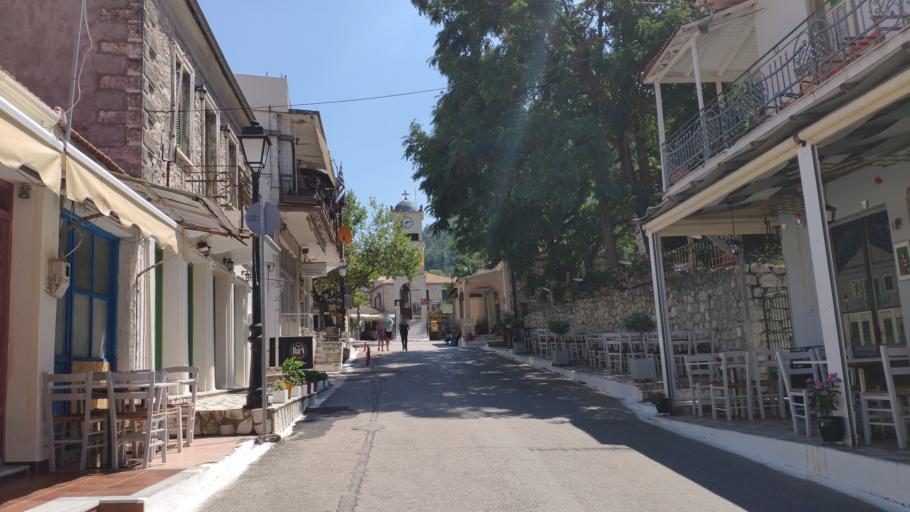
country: GR
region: Ionian Islands
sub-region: Lefkada
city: Nidri
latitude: 38.7594
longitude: 20.6488
